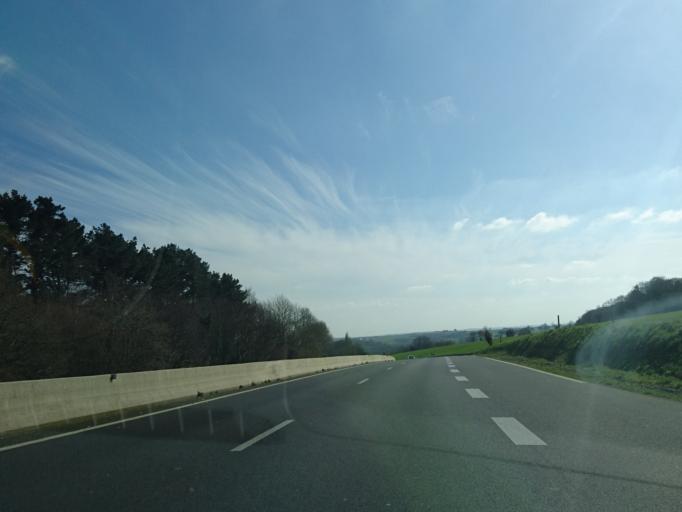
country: FR
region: Brittany
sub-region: Departement du Finistere
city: Daoulas
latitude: 48.3749
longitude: -4.2717
